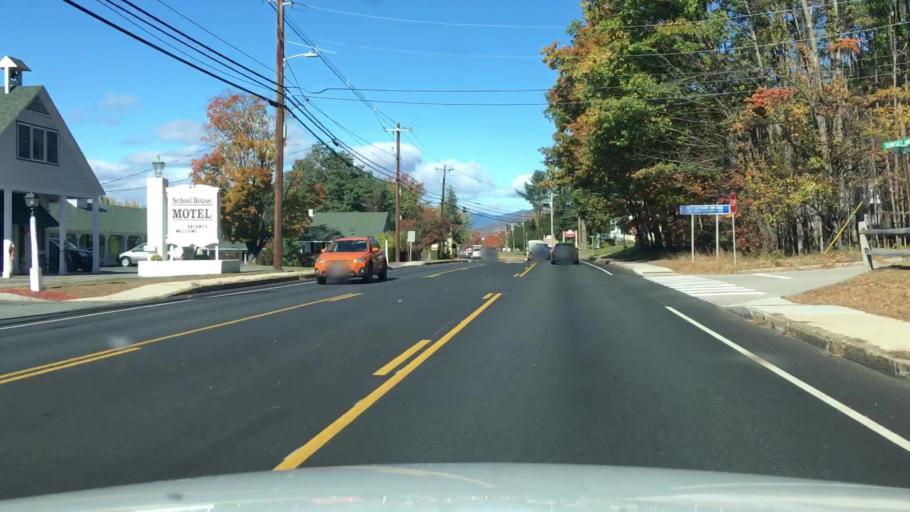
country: US
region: New Hampshire
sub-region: Carroll County
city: North Conway
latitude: 44.0381
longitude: -71.1226
